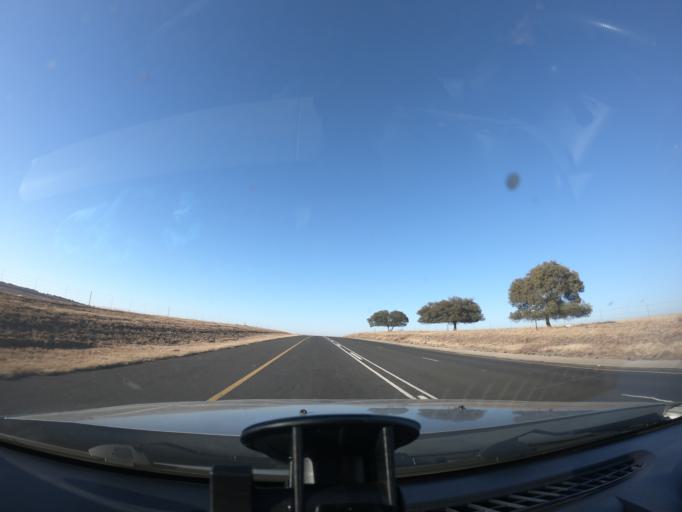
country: ZA
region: Mpumalanga
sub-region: Gert Sibande District Municipality
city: Ermelo
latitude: -26.4537
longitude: 29.9504
